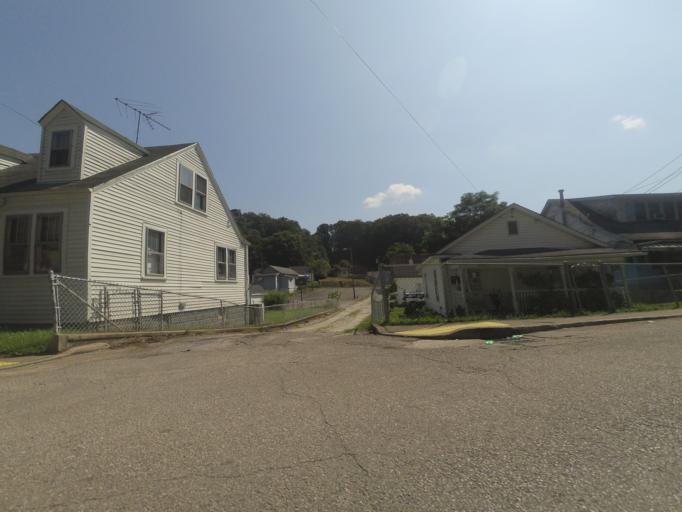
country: US
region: West Virginia
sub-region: Cabell County
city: Huntington
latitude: 38.4169
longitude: -82.4118
